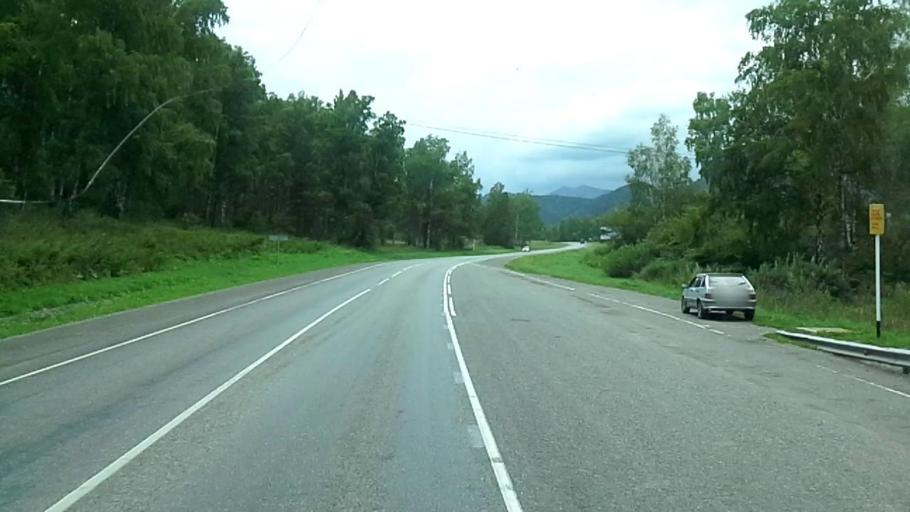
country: RU
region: Altay
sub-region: Mayminskiy Rayon
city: Manzherok
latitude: 51.8569
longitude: 85.7533
